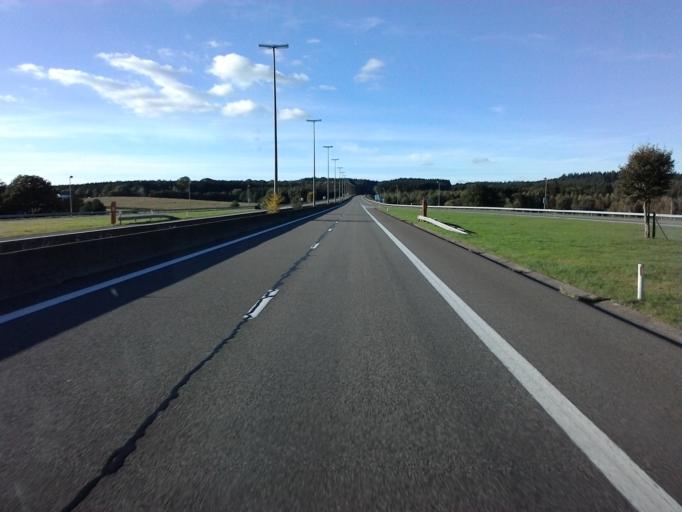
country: BE
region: Wallonia
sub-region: Province du Luxembourg
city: Houffalize
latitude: 50.1739
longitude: 5.7892
